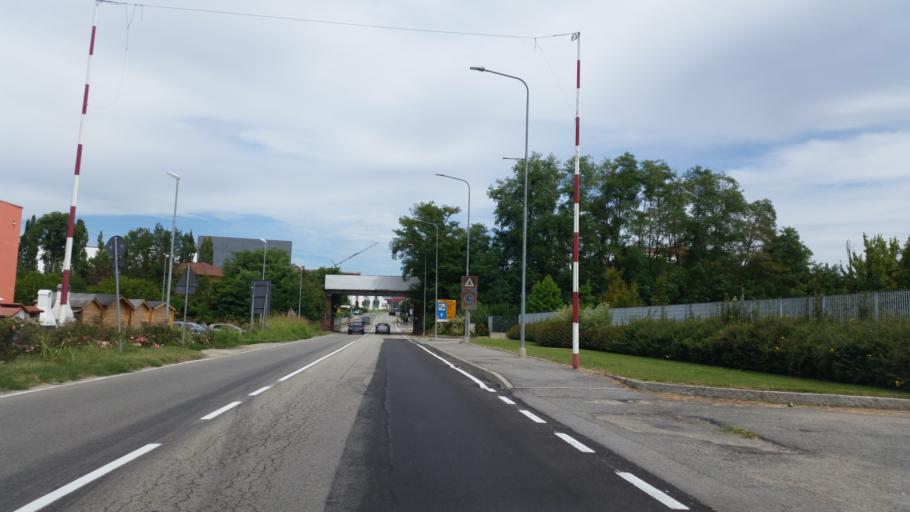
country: IT
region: Piedmont
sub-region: Provincia di Asti
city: Asti
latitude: 44.9052
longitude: 8.1817
